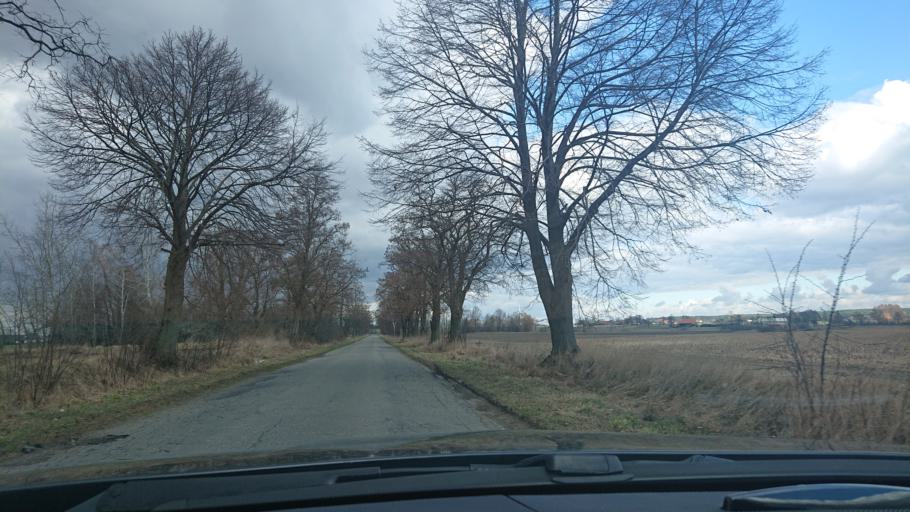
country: PL
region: Greater Poland Voivodeship
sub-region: Powiat gnieznienski
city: Trzemeszno
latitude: 52.5774
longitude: 17.7090
